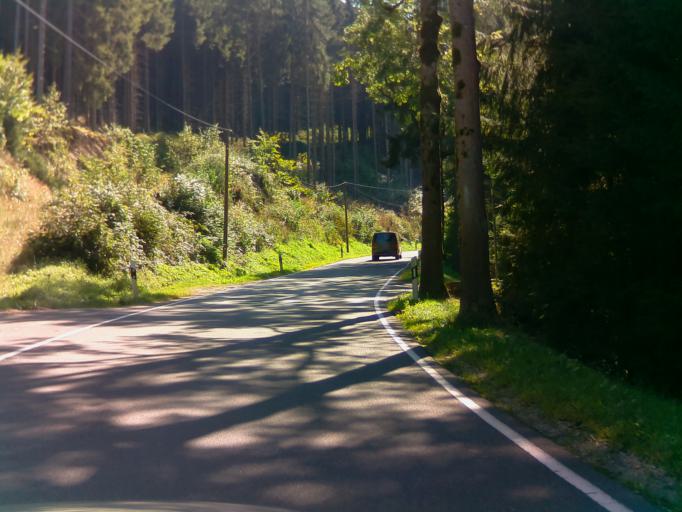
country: DE
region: Thuringia
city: Leutenberg
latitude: 50.5199
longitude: 11.4826
